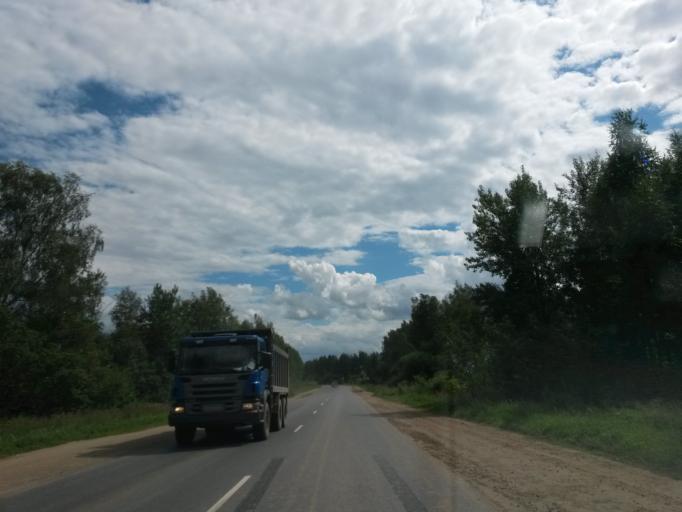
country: RU
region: Ivanovo
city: Novo-Talitsy
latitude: 57.0286
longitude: 40.7553
